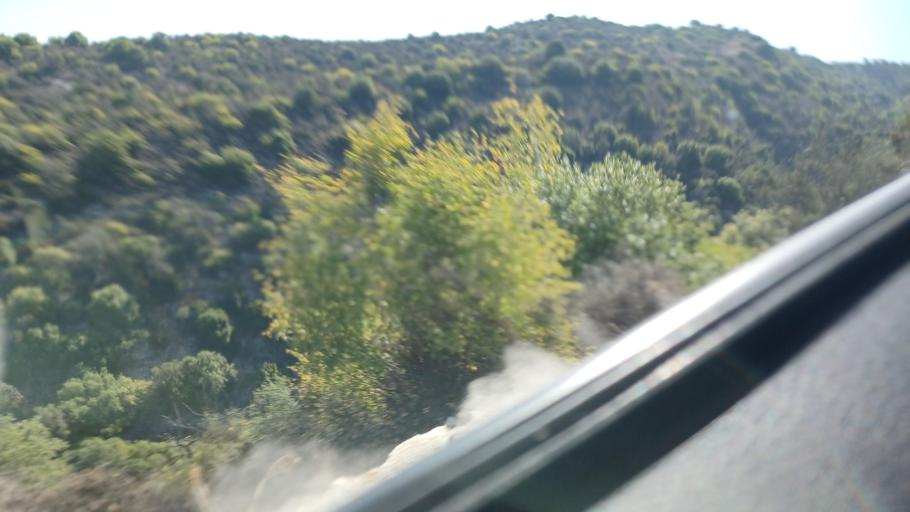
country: CY
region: Pafos
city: Tala
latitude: 34.8670
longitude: 32.4404
